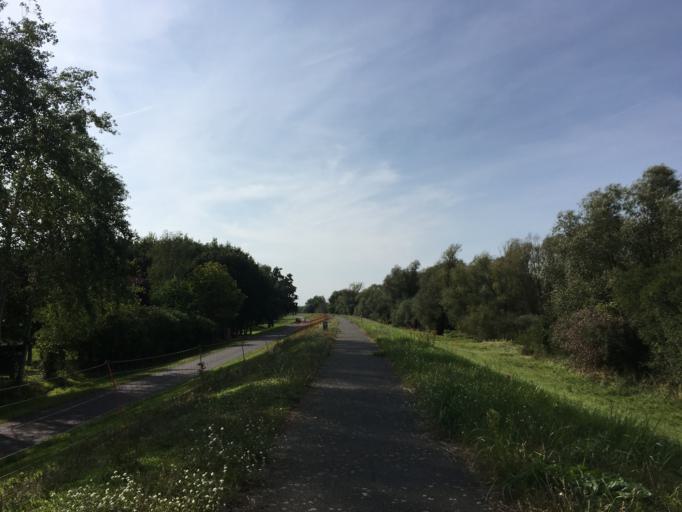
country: DE
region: Brandenburg
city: Ziltendorf
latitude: 52.2605
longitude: 14.6603
